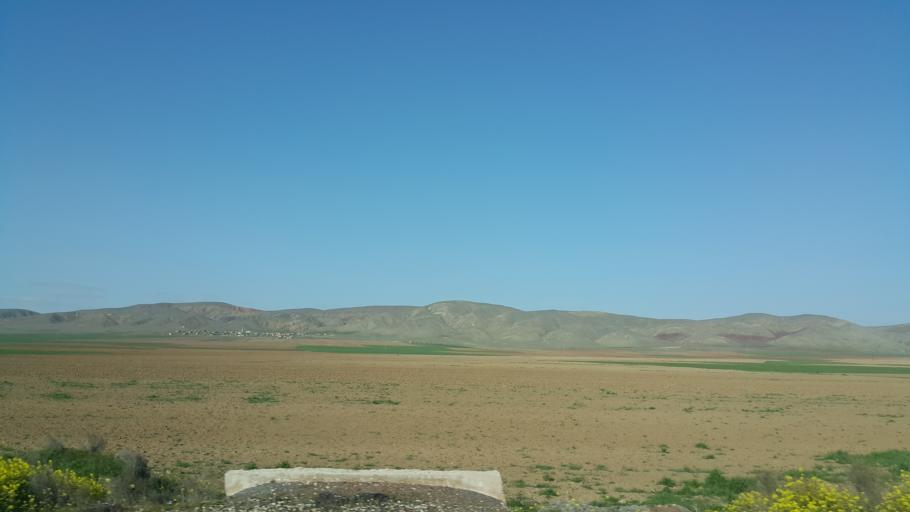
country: TR
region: Aksaray
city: Acipinar
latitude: 38.6508
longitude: 33.7246
